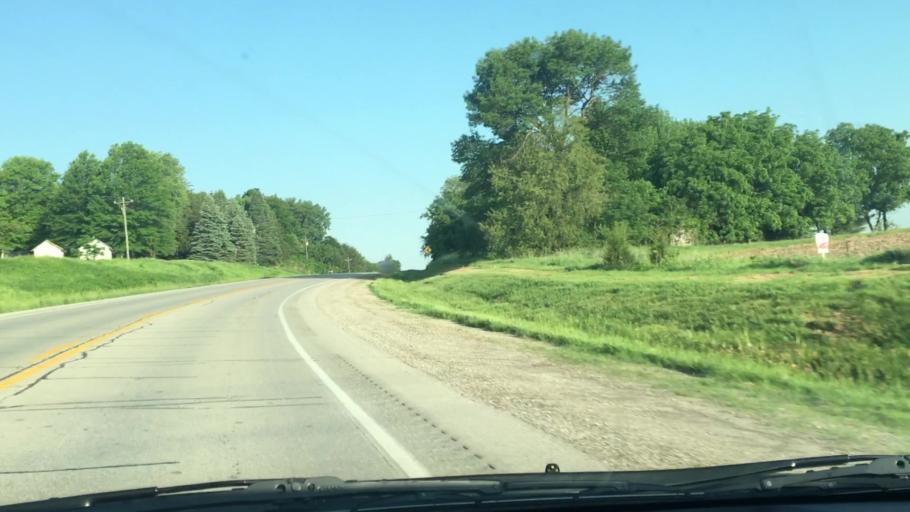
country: US
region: Iowa
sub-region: Johnson County
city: Tiffin
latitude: 41.7092
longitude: -91.6866
